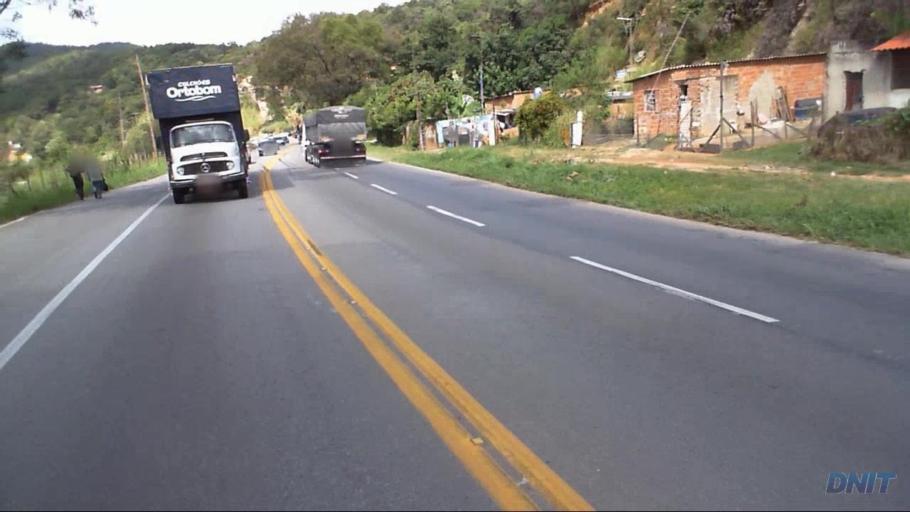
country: BR
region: Minas Gerais
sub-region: Santa Luzia
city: Santa Luzia
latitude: -19.8231
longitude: -43.8259
